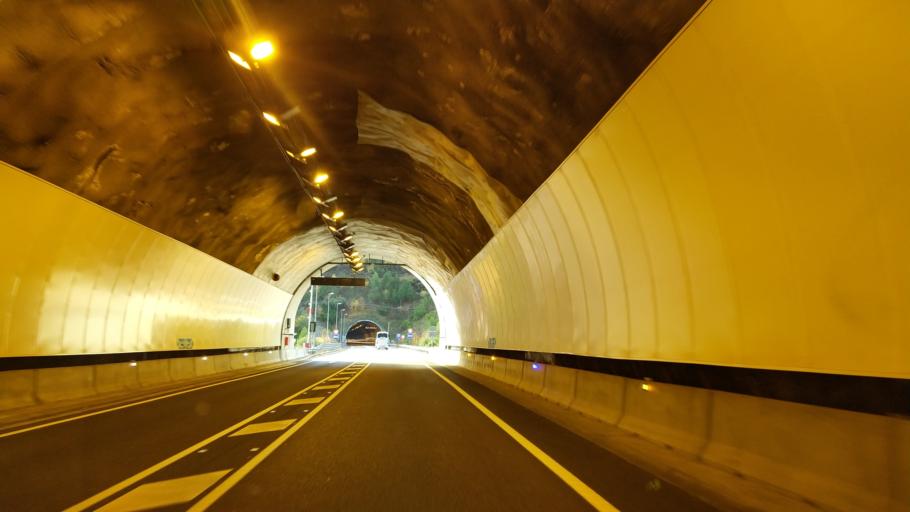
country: ES
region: Catalonia
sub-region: Provincia de Lleida
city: Coll de Nargo
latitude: 42.1466
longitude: 1.3069
